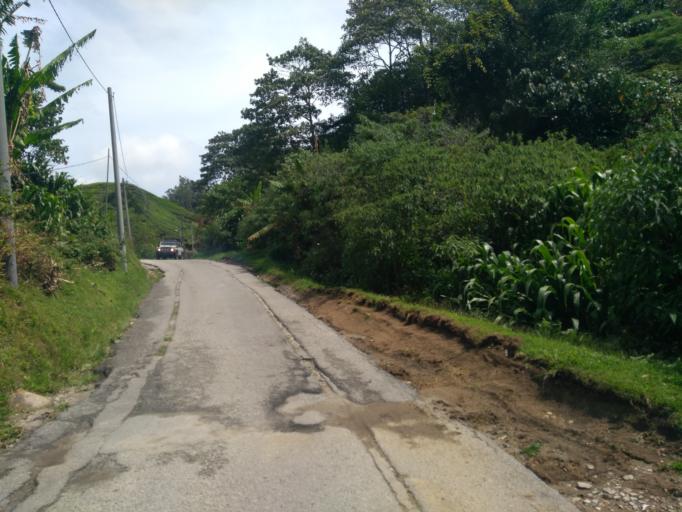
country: MY
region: Pahang
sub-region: Cameron Highlands
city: Tanah Rata
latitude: 4.5200
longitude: 101.4049
